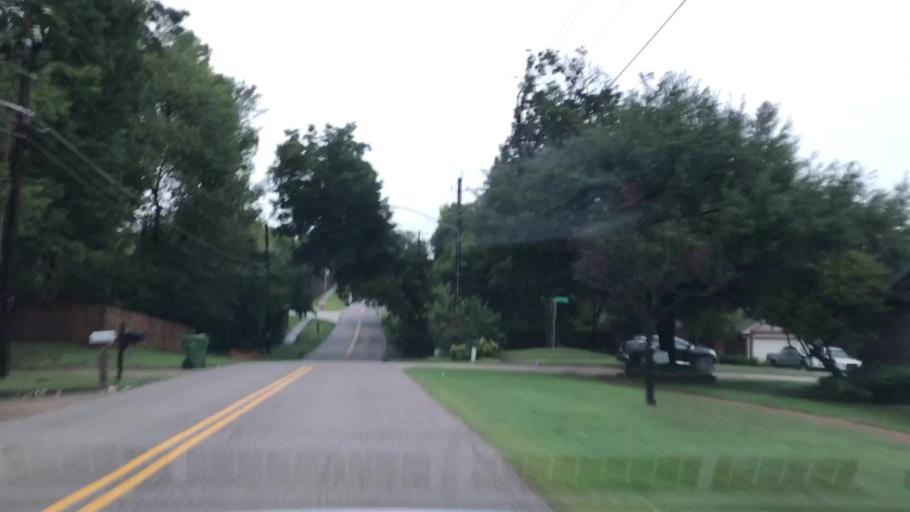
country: US
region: Texas
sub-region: Collin County
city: Plano
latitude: 32.9702
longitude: -96.6702
